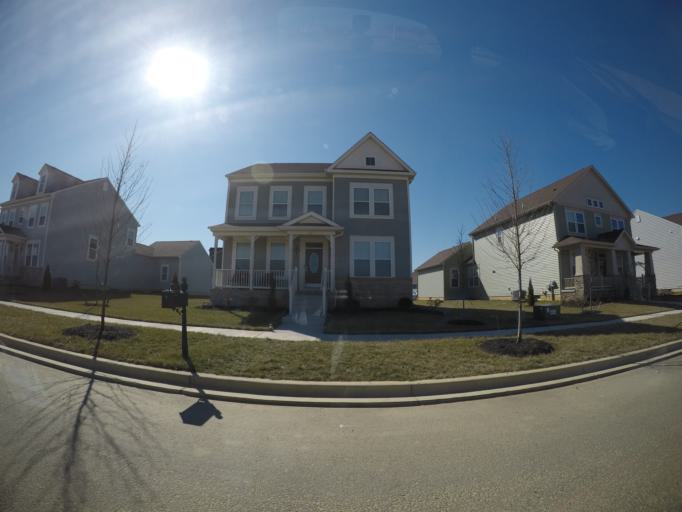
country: US
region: Delaware
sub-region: New Castle County
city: Middletown
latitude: 39.5155
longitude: -75.6677
